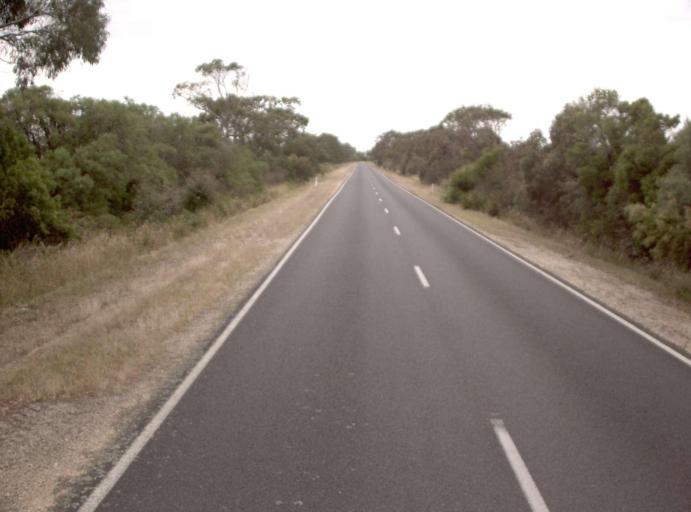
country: AU
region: Victoria
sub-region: Wellington
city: Sale
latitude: -38.2002
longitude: 147.3323
